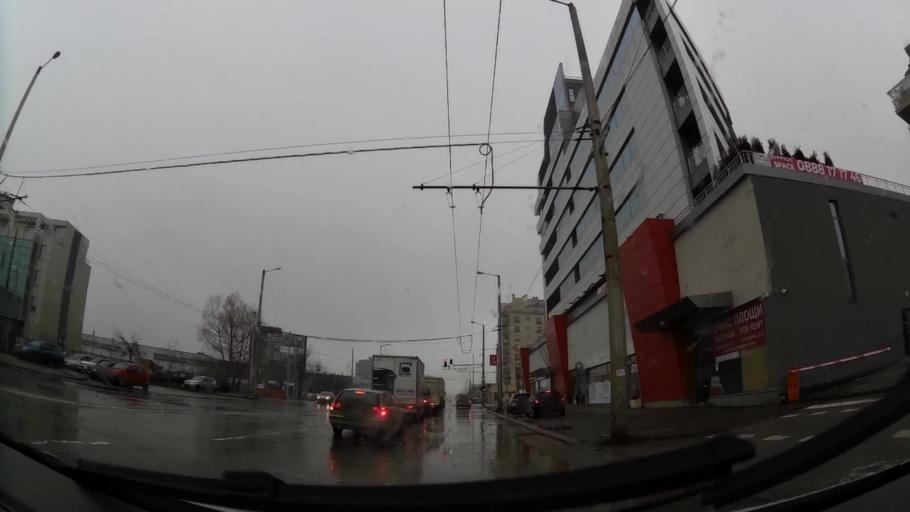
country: BG
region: Sofia-Capital
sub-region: Stolichna Obshtina
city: Sofia
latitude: 42.6519
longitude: 23.4049
